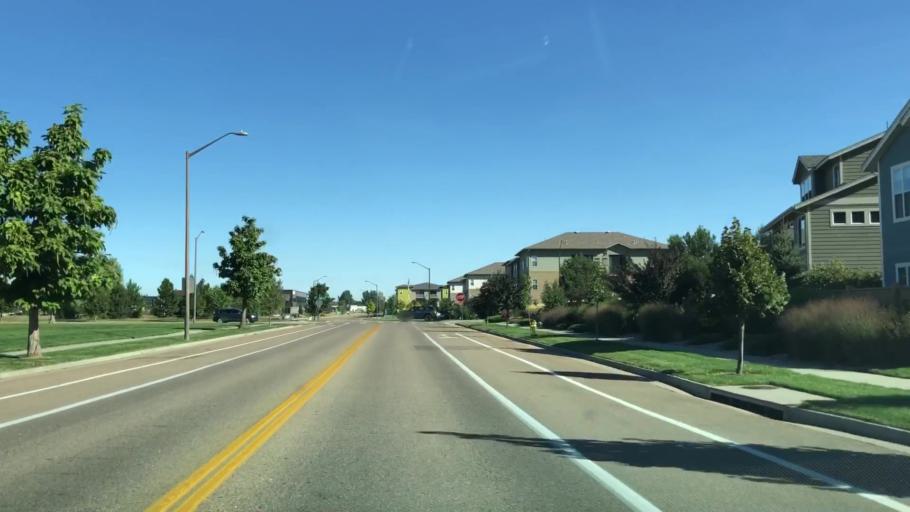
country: US
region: Colorado
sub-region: Larimer County
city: Fort Collins
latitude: 40.5152
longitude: -105.0105
